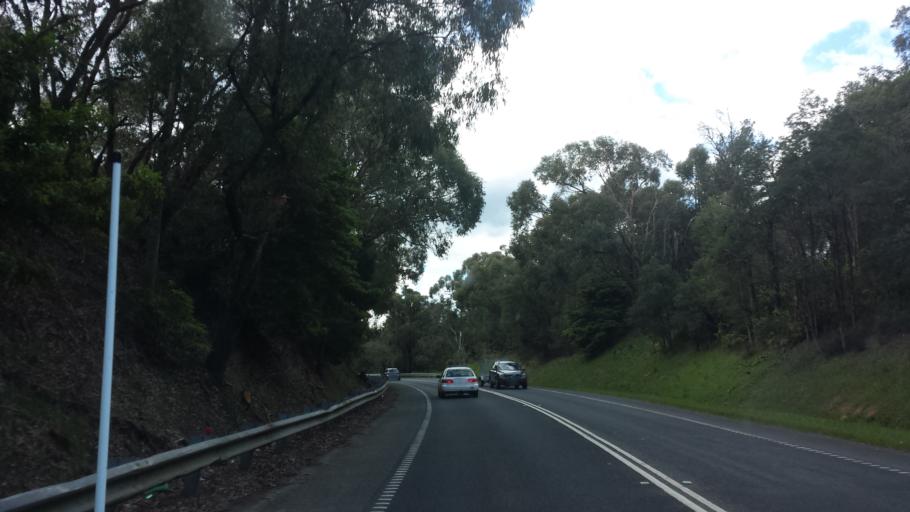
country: AU
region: Victoria
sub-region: Yarra Ranges
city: Selby
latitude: -37.9549
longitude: 145.3840
